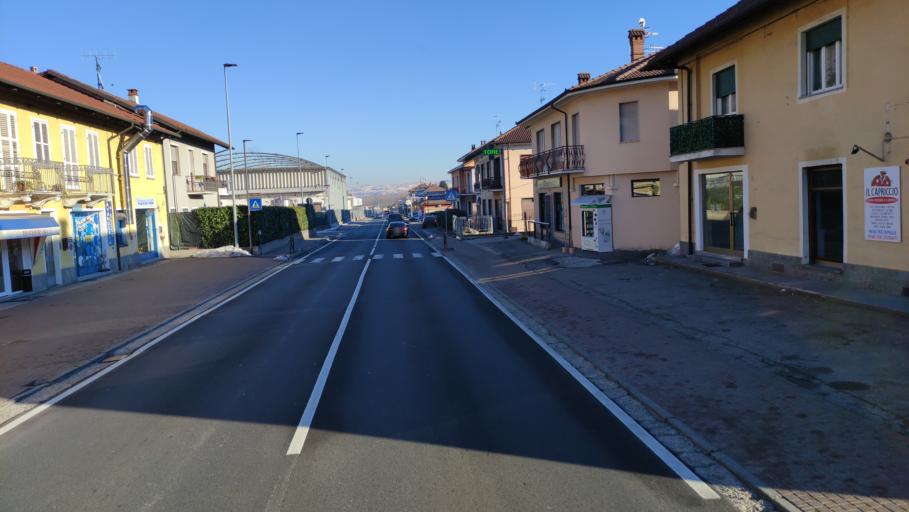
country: IT
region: Piedmont
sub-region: Provincia di Cuneo
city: Cinzano
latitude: 44.6935
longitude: 7.9199
